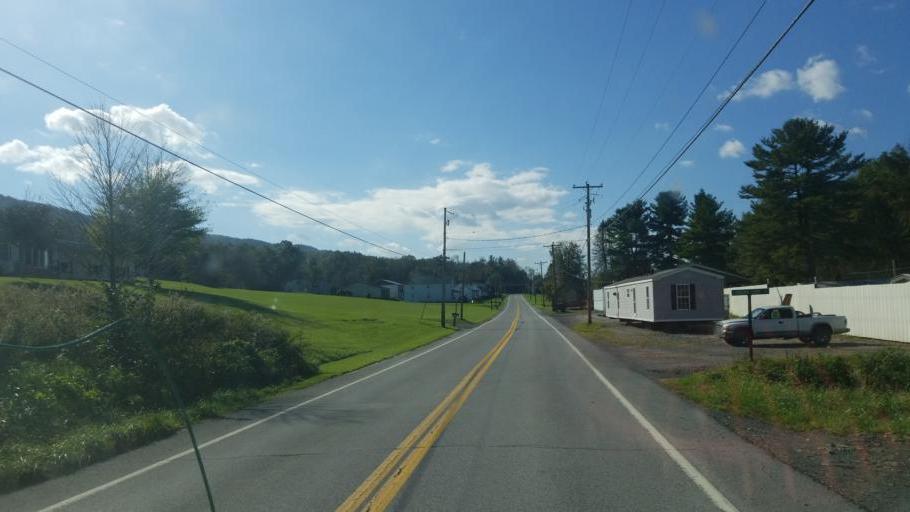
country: US
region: Pennsylvania
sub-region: Blair County
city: Claysburg
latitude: 40.2524
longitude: -78.4624
